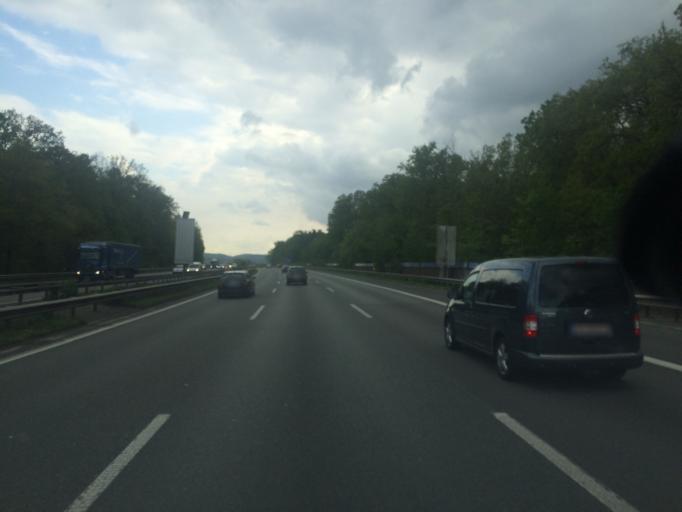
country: DE
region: North Rhine-Westphalia
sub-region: Regierungsbezirk Detmold
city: Leopoldshohe
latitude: 52.0335
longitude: 8.6396
